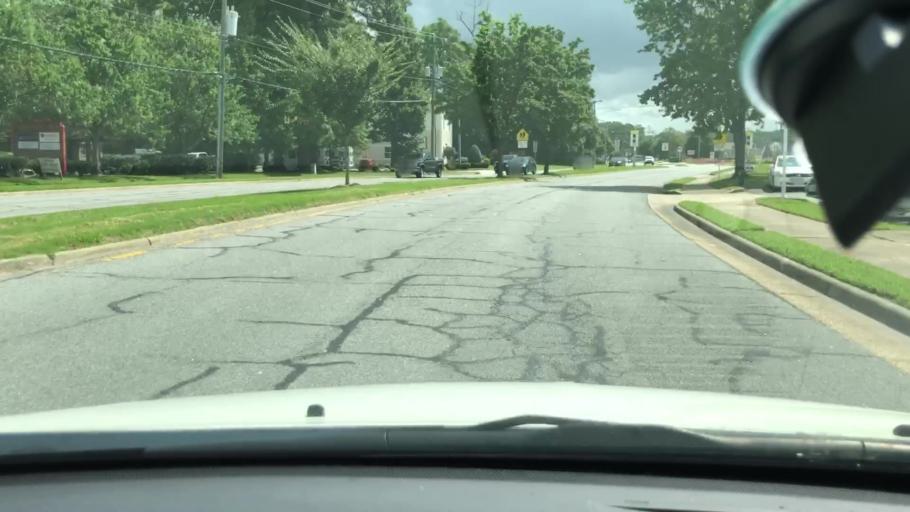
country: US
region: Virginia
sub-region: City of Chesapeake
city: Chesapeake
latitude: 36.8129
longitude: -76.2042
